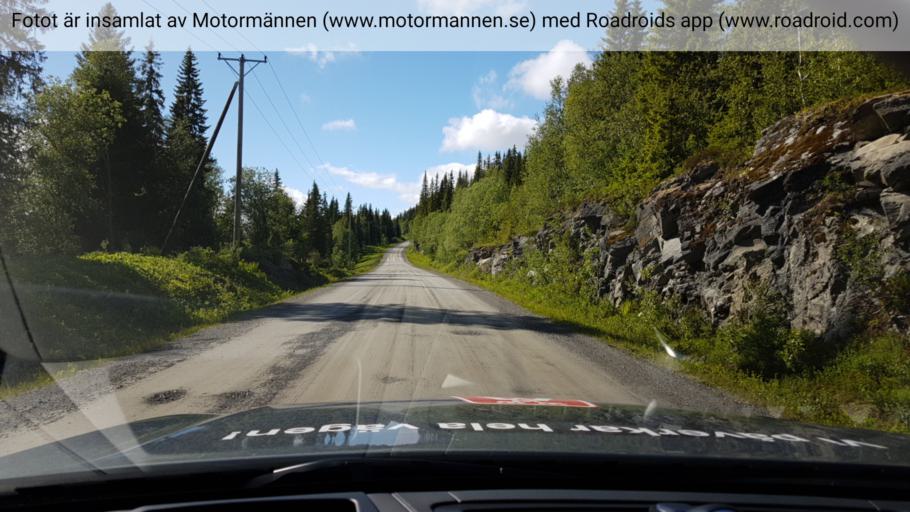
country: SE
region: Jaemtland
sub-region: Are Kommun
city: Are
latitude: 63.6940
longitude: 12.7967
